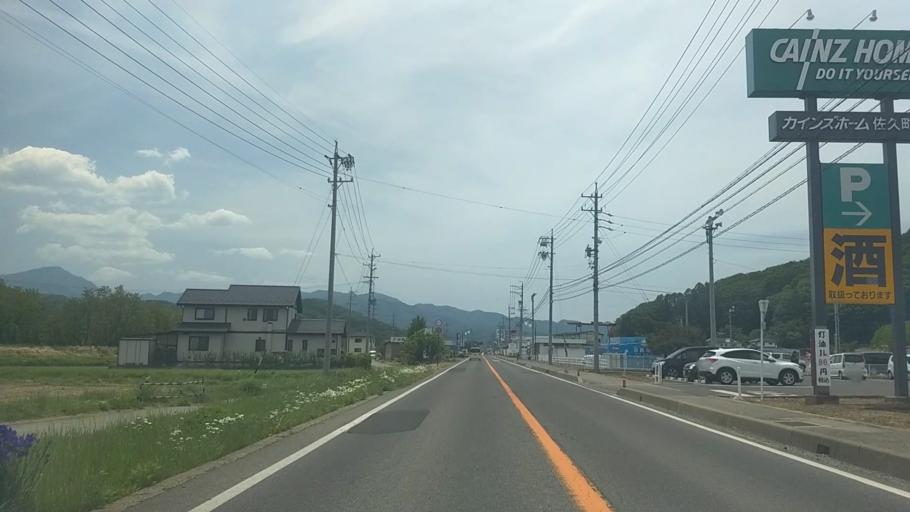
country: JP
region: Nagano
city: Saku
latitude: 36.1745
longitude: 138.4852
